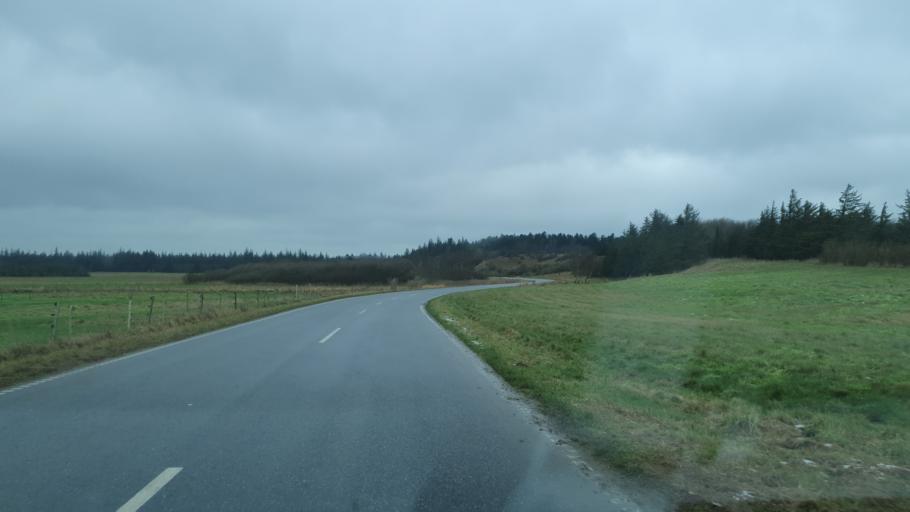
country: DK
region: North Denmark
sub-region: Jammerbugt Kommune
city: Fjerritslev
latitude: 57.1121
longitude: 9.1280
